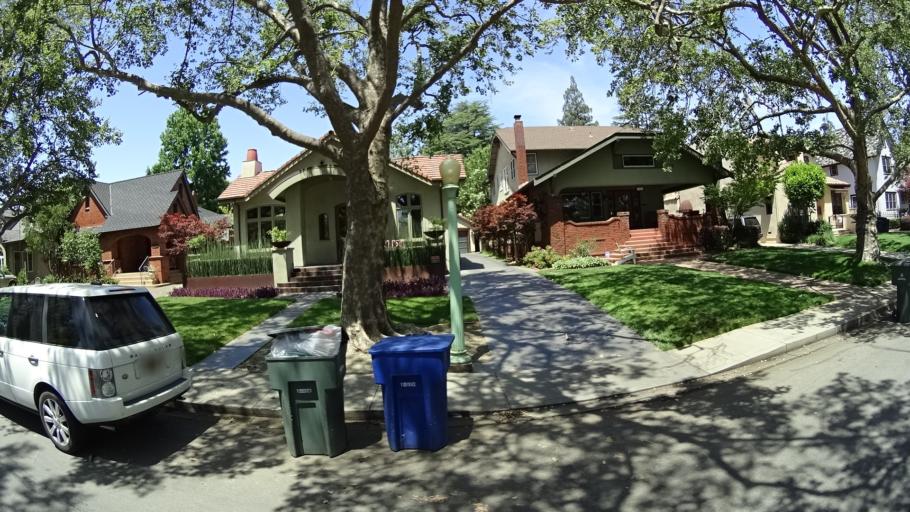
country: US
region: California
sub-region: Sacramento County
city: Sacramento
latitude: 38.5668
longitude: -121.4453
